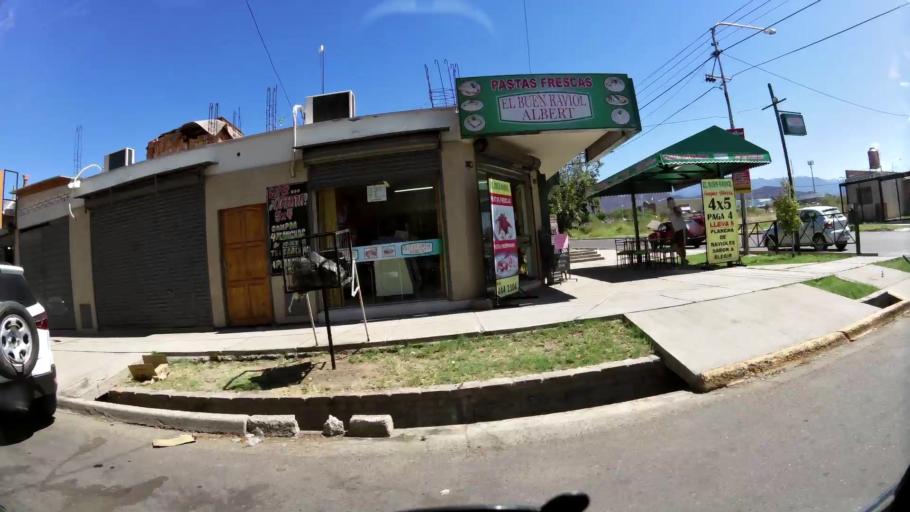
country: AR
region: Mendoza
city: Las Heras
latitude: -32.8519
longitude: -68.8559
